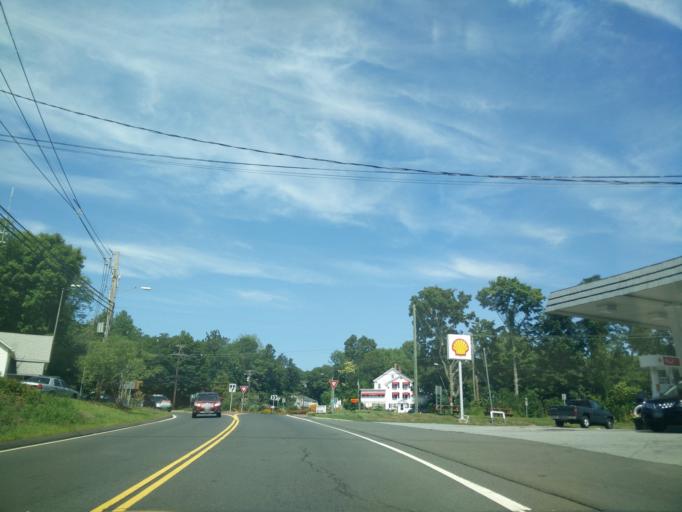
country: US
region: Connecticut
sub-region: New Haven County
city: Madison
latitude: 41.3574
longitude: -72.5645
